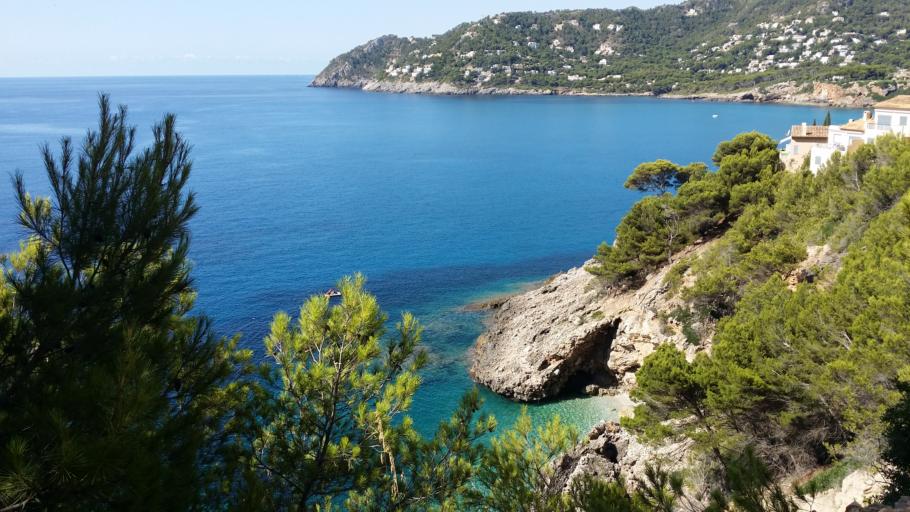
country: ES
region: Balearic Islands
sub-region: Illes Balears
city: Capdepera
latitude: 39.6566
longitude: 3.4490
